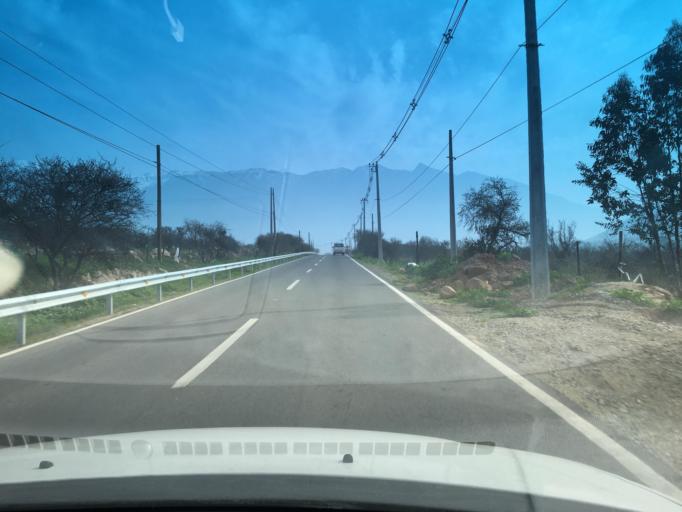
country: CL
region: Santiago Metropolitan
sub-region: Provincia de Chacabuco
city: Lampa
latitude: -33.2531
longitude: -70.9068
